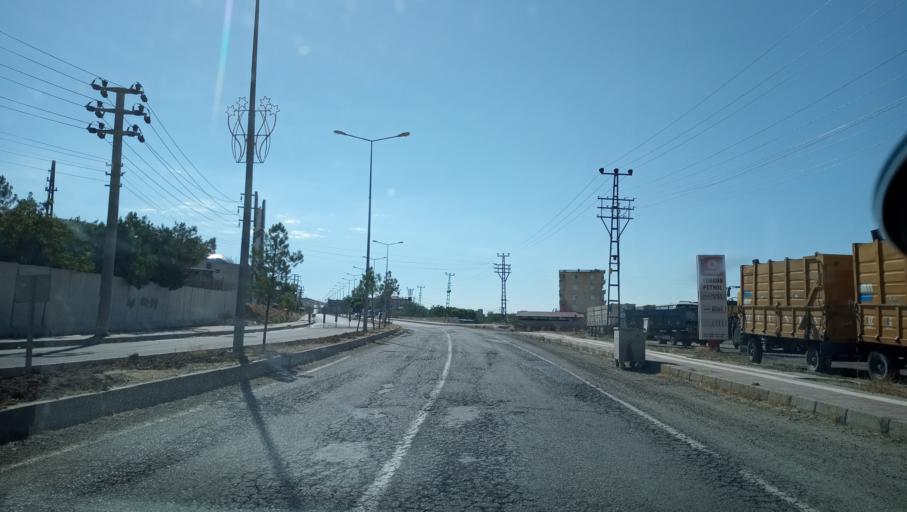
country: TR
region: Diyarbakir
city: Silvan
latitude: 38.1364
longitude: 41.0245
